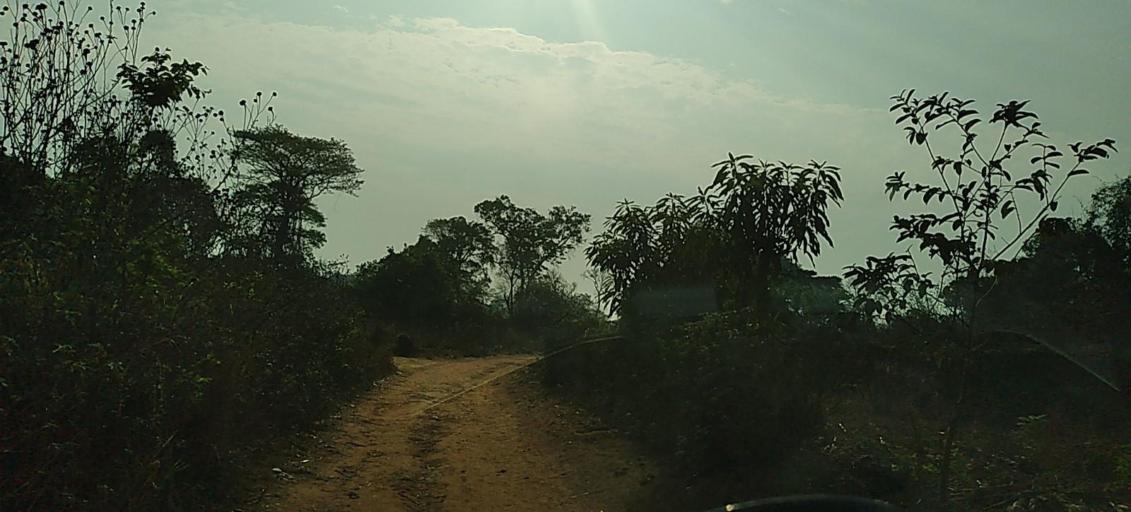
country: ZM
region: North-Western
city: Solwezi
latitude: -12.3529
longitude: 26.5363
